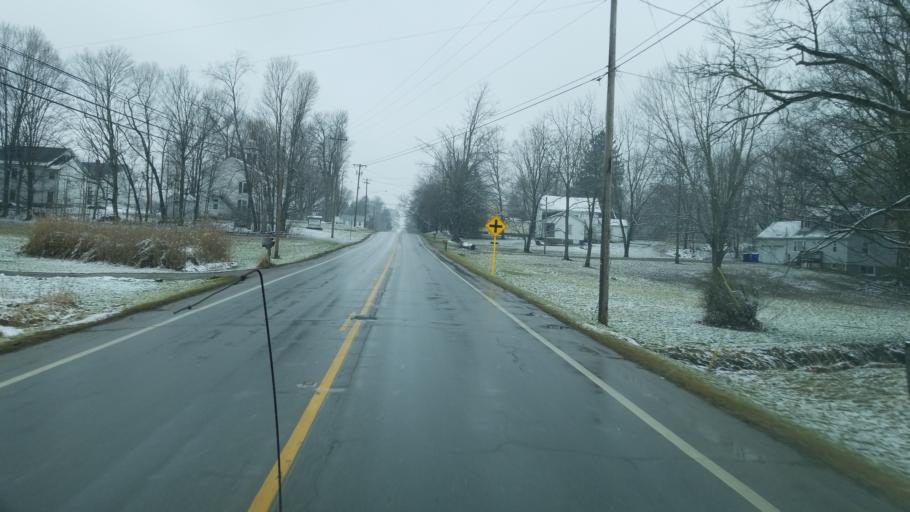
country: US
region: Ohio
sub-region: Portage County
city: Mantua
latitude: 41.3099
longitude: -81.2423
